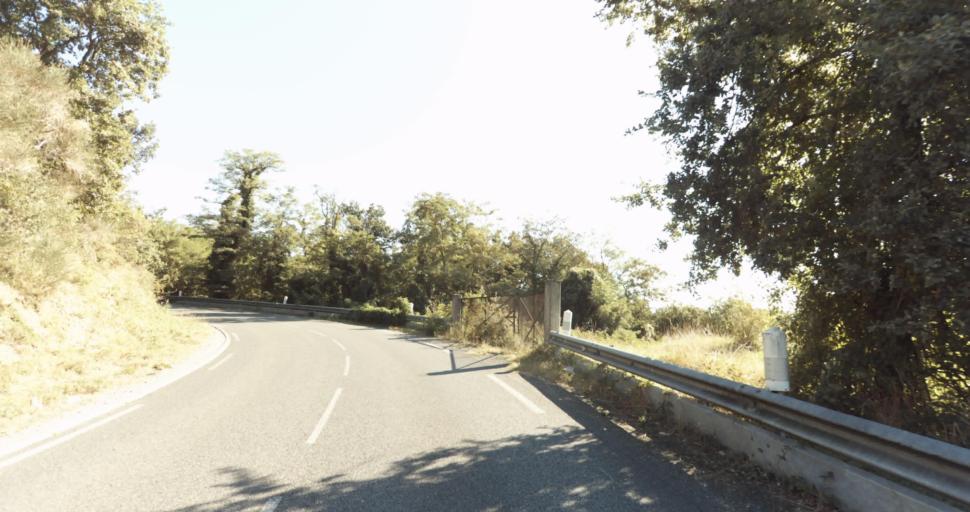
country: FR
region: Midi-Pyrenees
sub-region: Departement de la Haute-Garonne
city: L'Union
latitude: 43.6729
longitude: 1.4775
